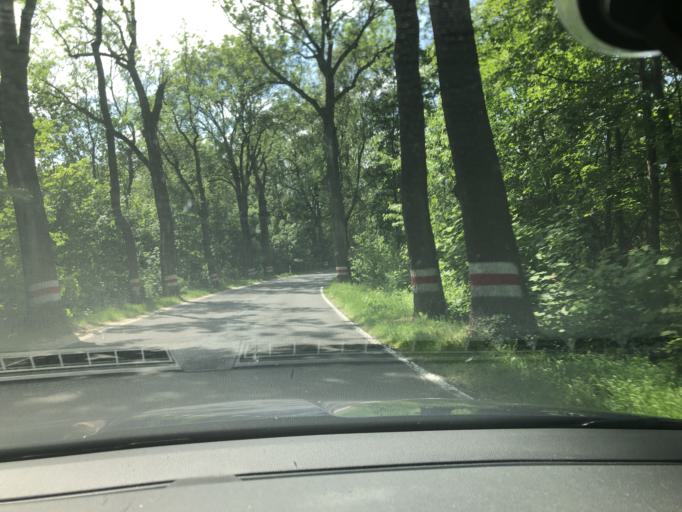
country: PL
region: Lower Silesian Voivodeship
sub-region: Powiat zlotoryjski
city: Swierzawa
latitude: 50.9636
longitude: 15.8431
